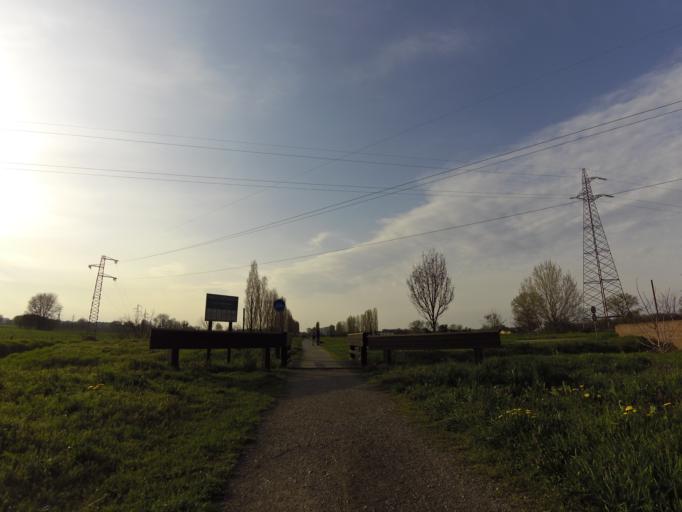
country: IT
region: Lombardy
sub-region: Citta metropolitana di Milano
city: Chiaravalle
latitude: 45.4194
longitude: 9.2326
